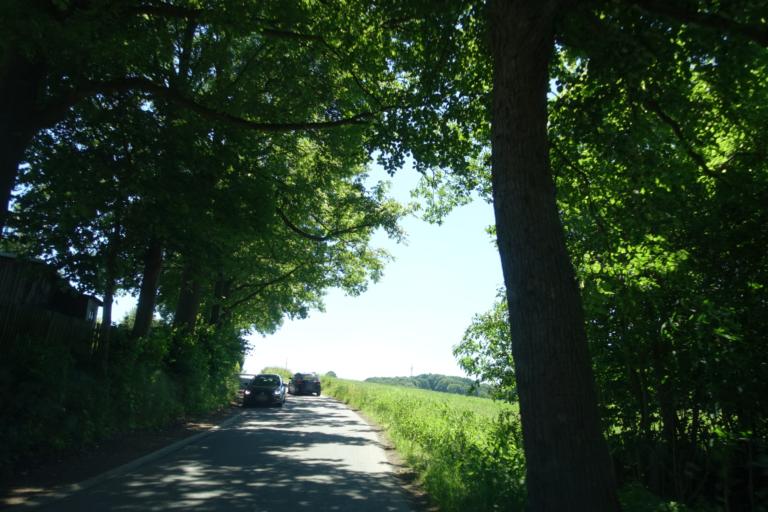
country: DE
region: Saxony
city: Borstendorf
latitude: 50.7765
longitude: 13.1775
